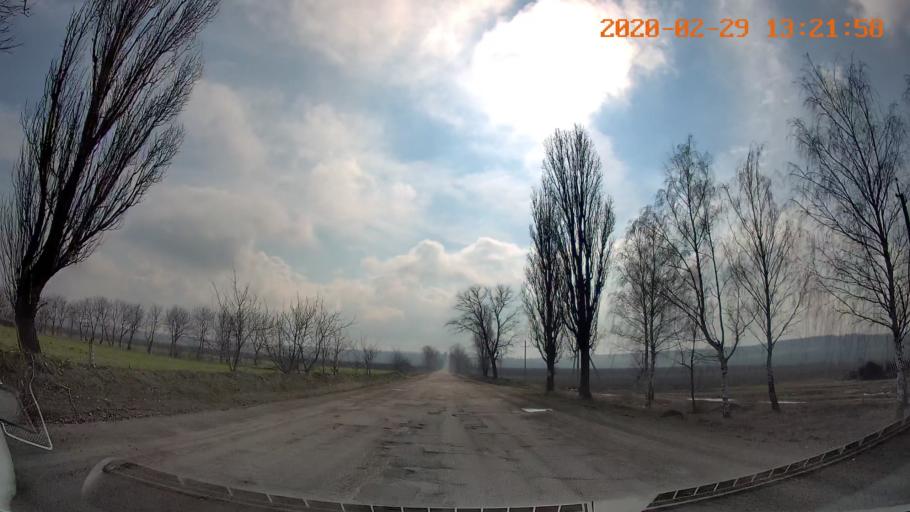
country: MD
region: Telenesti
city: Camenca
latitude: 47.9655
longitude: 28.6288
